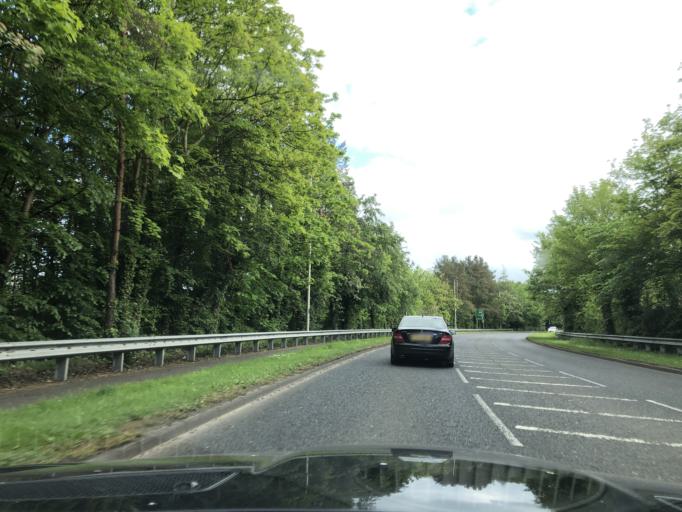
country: GB
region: Northern Ireland
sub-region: Antrim Borough
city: Antrim
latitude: 54.7109
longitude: -6.2194
